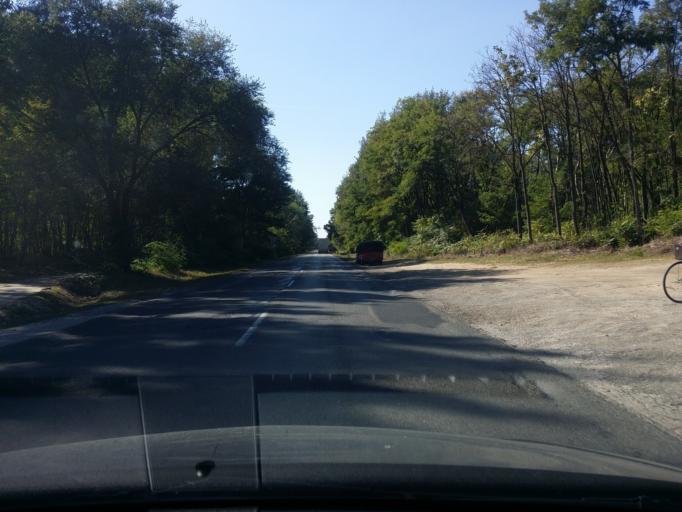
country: HU
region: Bacs-Kiskun
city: Lakitelek
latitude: 46.8746
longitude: 19.9752
